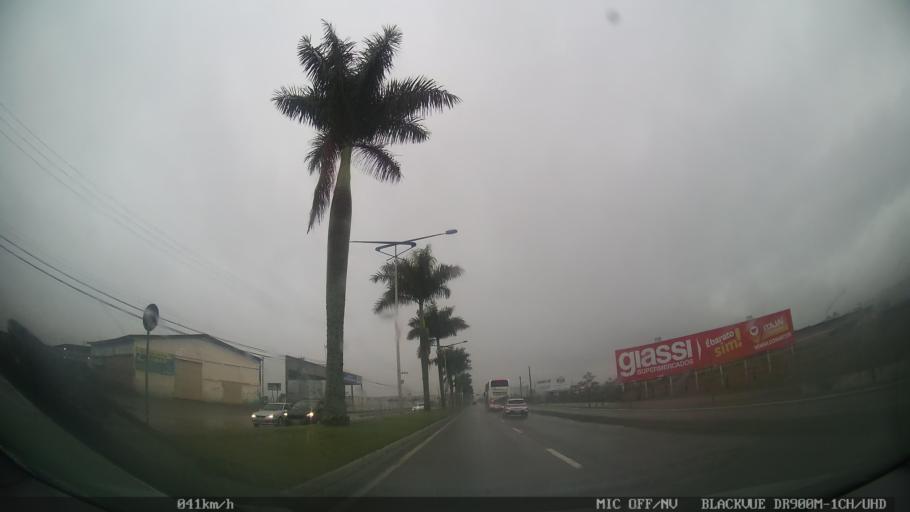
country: BR
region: Santa Catarina
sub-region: Itajai
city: Itajai
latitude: -26.9153
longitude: -48.6993
